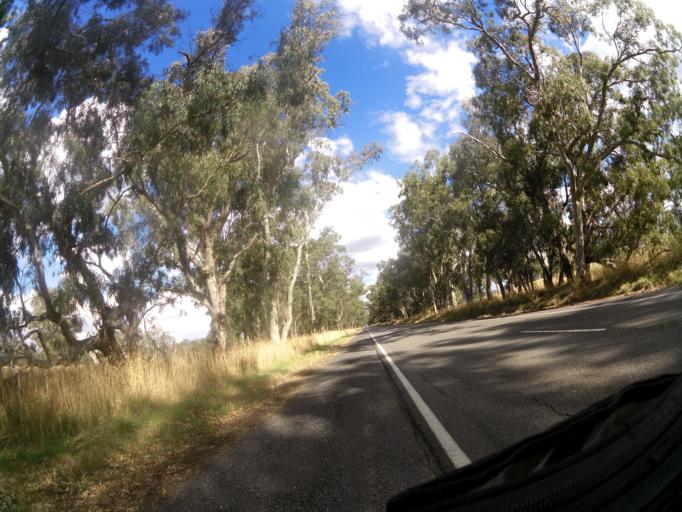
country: AU
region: Victoria
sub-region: Mansfield
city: Mansfield
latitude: -37.0082
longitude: 146.0824
